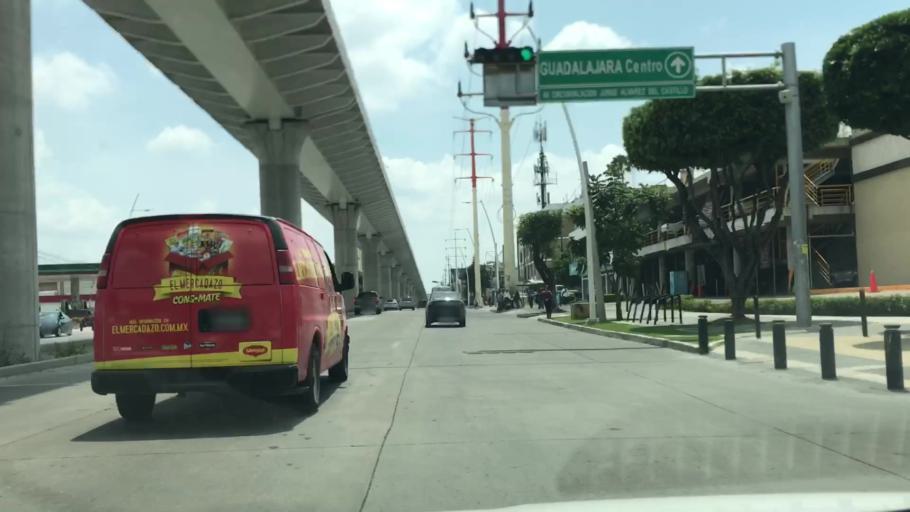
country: MX
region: Jalisco
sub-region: Zapopan
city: Zapopan
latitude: 20.7053
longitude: -103.3643
